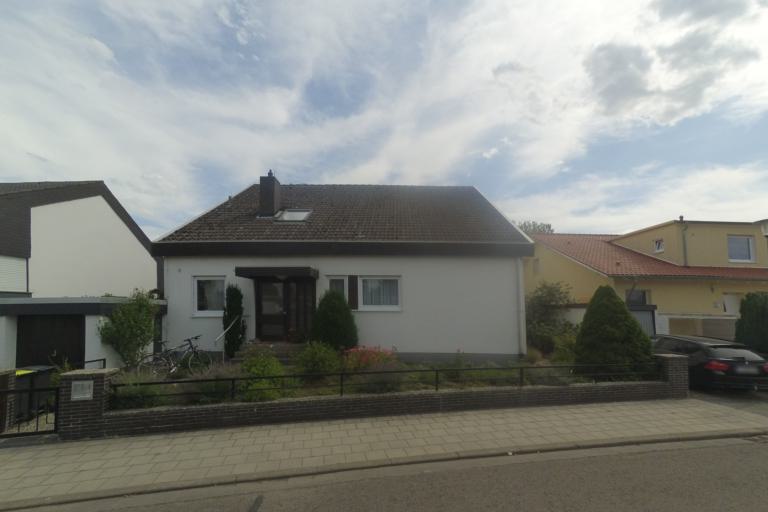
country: DE
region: Rheinland-Pfalz
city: Frankenthal
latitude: 49.5109
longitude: 8.3285
